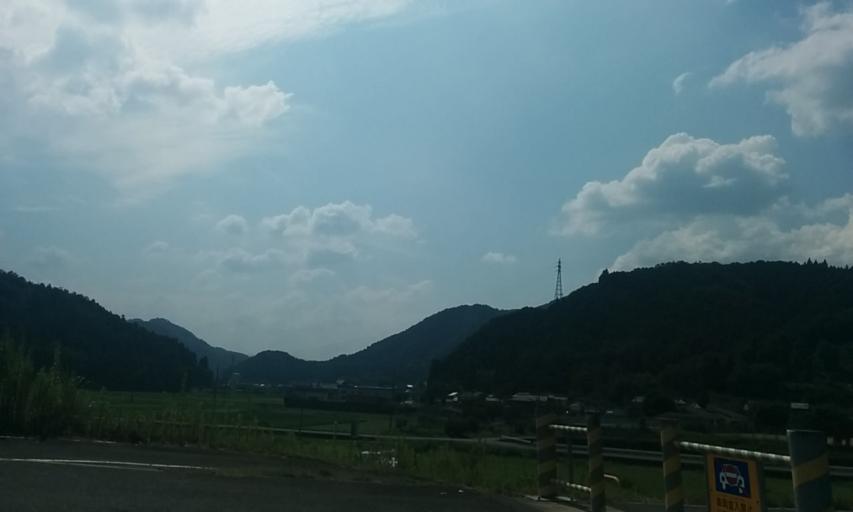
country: JP
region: Kyoto
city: Fukuchiyama
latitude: 35.3406
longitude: 135.1097
